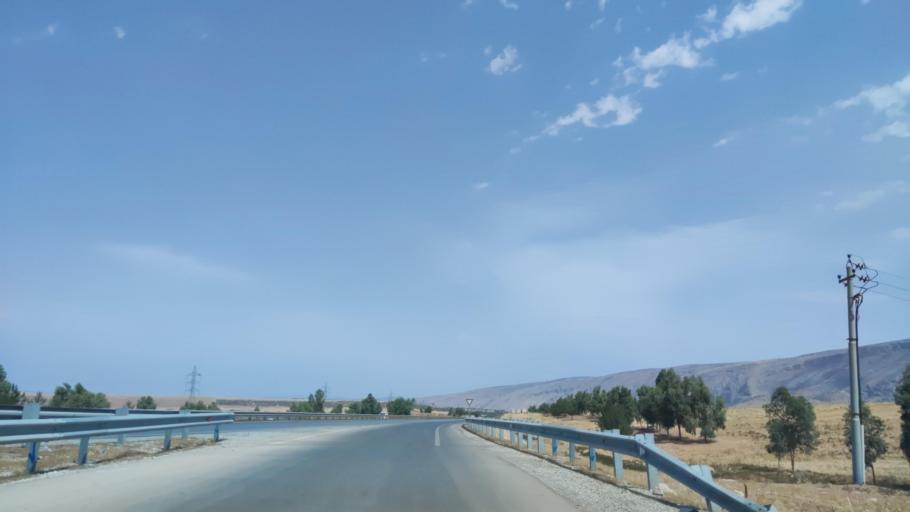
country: IQ
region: Arbil
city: Shaqlawah
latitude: 36.4586
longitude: 44.3845
